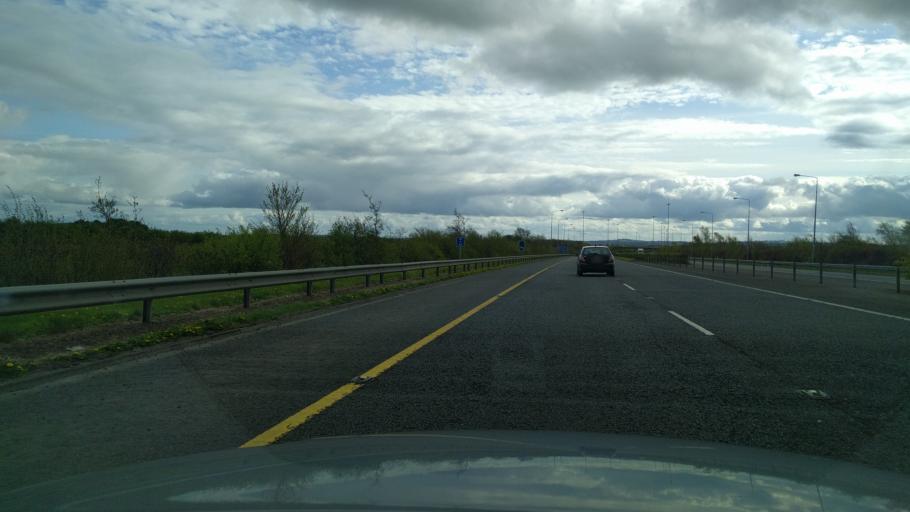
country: IE
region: Leinster
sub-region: Lu
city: Dromiskin
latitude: 53.9084
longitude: -6.4175
